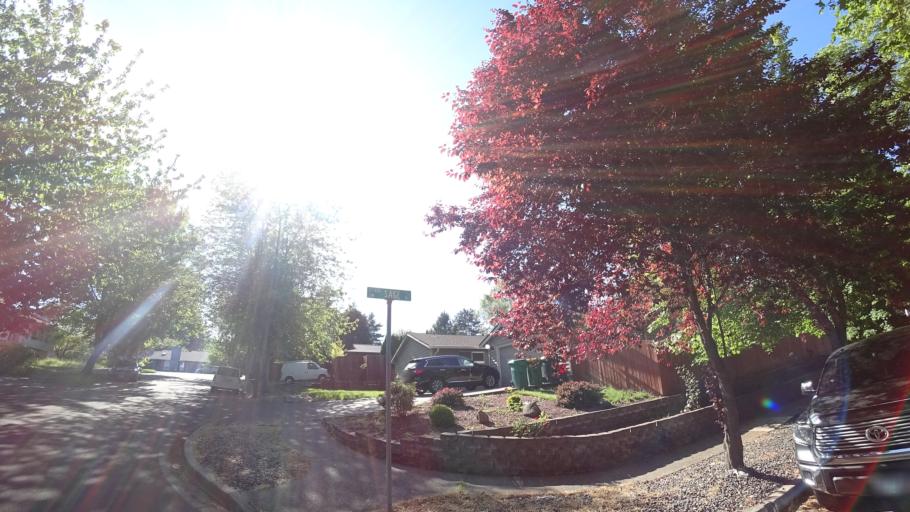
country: US
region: Oregon
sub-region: Washington County
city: Beaverton
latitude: 45.4642
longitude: -122.8072
